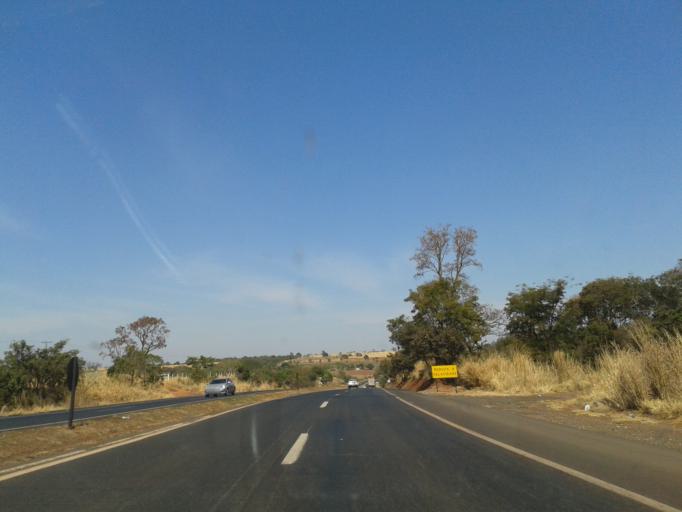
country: BR
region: Minas Gerais
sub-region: Monte Alegre De Minas
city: Monte Alegre de Minas
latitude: -18.8207
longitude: -49.0877
